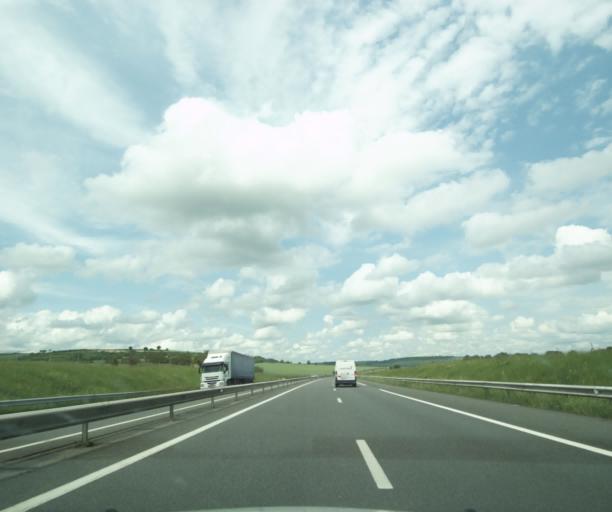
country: FR
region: Auvergne
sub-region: Departement de l'Allier
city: Ebreuil
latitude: 46.1484
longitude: 3.1154
